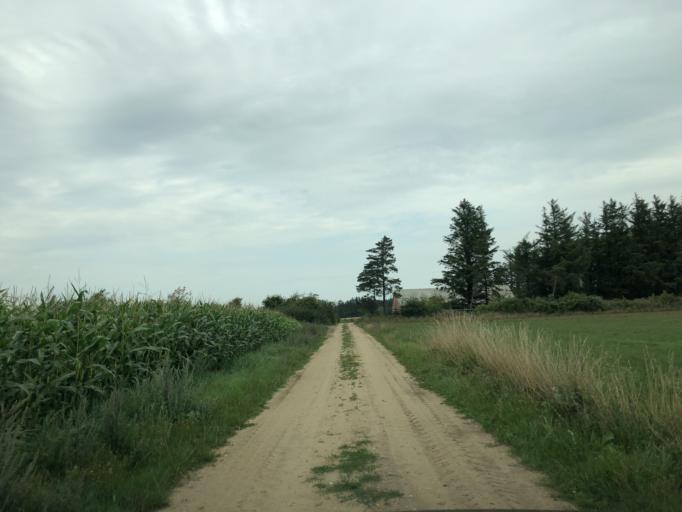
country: DK
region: Central Jutland
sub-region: Holstebro Kommune
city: Ulfborg
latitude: 56.2363
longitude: 8.3574
